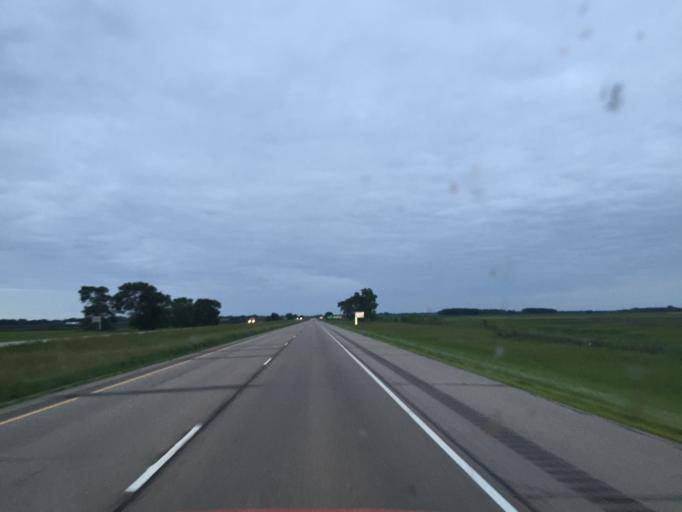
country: US
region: Minnesota
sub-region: Mower County
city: Austin
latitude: 43.6596
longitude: -93.0525
